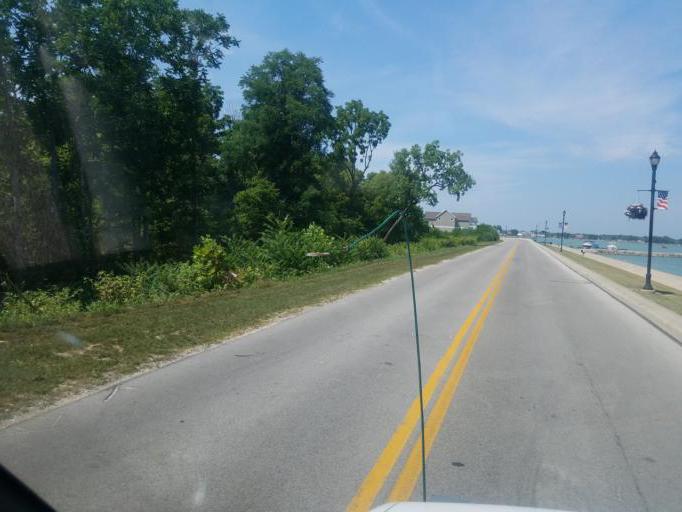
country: US
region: Ohio
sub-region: Mercer County
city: Celina
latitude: 40.5297
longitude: -84.5740
